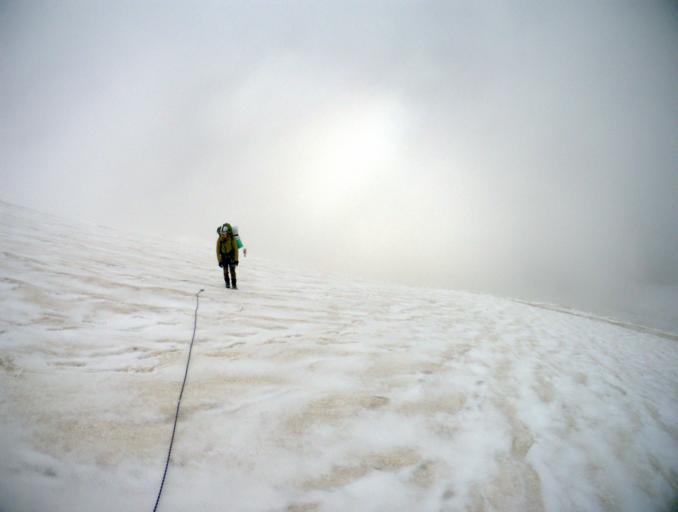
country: RU
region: Kabardino-Balkariya
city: Terskol
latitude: 43.3663
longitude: 42.4910
